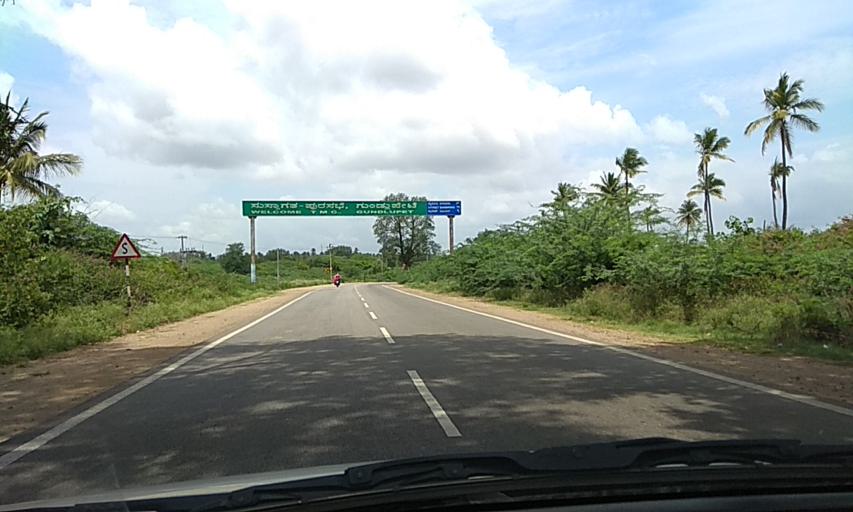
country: IN
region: Karnataka
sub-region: Chamrajnagar
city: Gundlupet
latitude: 11.8108
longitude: 76.7074
